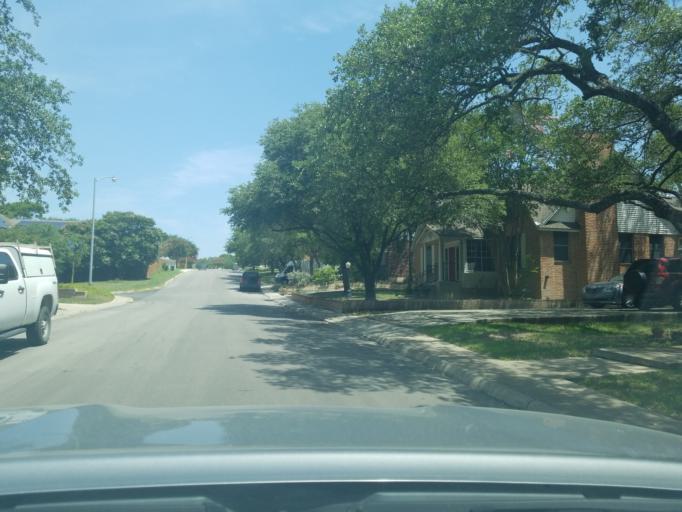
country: US
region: Texas
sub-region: Bexar County
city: Hollywood Park
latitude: 29.6428
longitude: -98.4936
